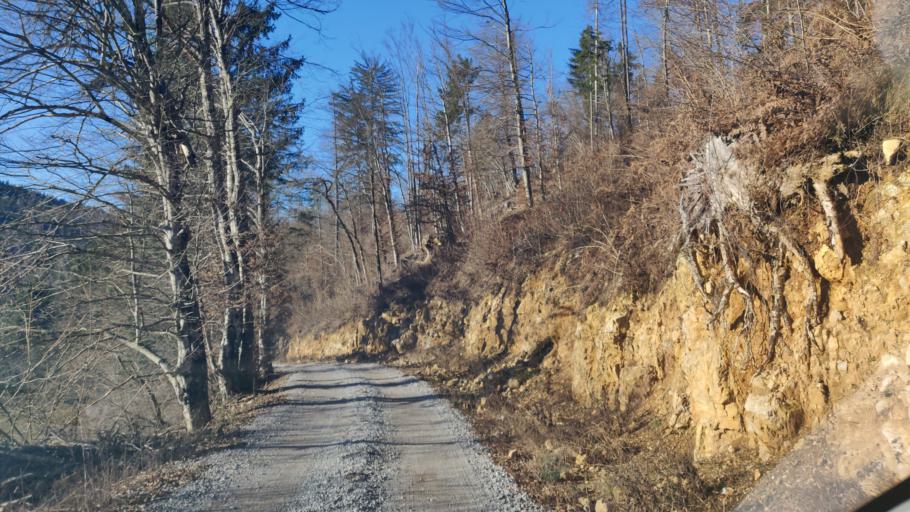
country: SI
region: Logatec
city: Logatec
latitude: 45.8710
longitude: 14.2202
